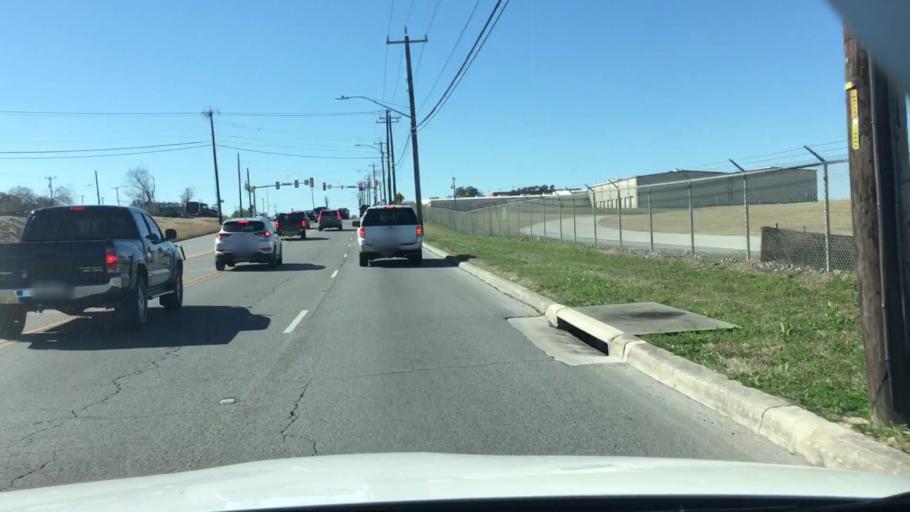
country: US
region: Texas
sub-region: Bexar County
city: Alamo Heights
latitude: 29.5385
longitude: -98.4477
